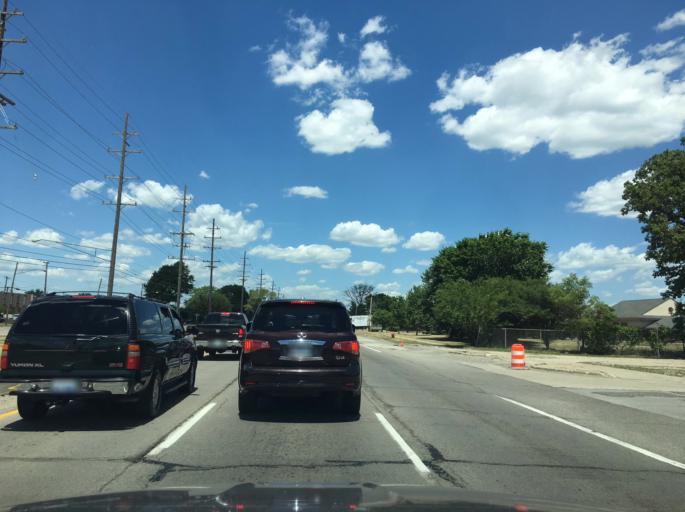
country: US
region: Michigan
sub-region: Macomb County
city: Warren
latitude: 42.4695
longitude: -83.0449
